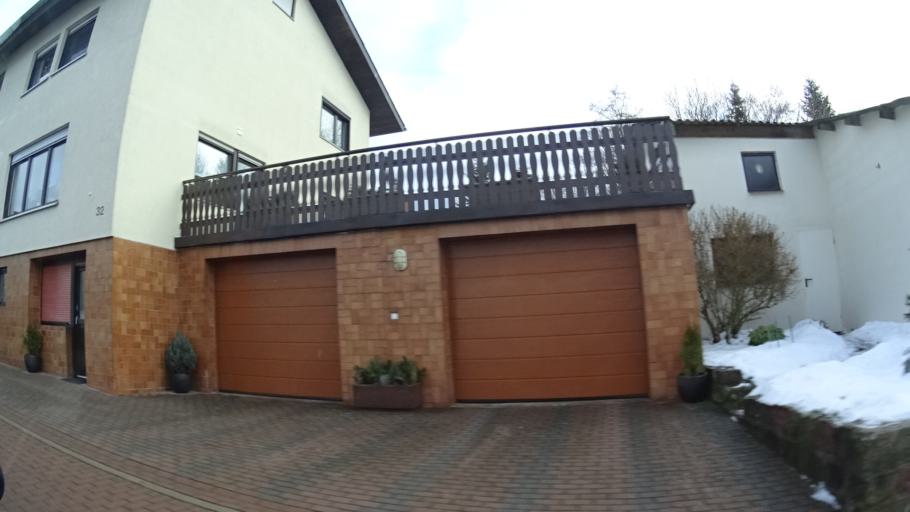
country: DE
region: Baden-Wuerttemberg
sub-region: Karlsruhe Region
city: Limbach
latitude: 49.4802
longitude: 9.1724
